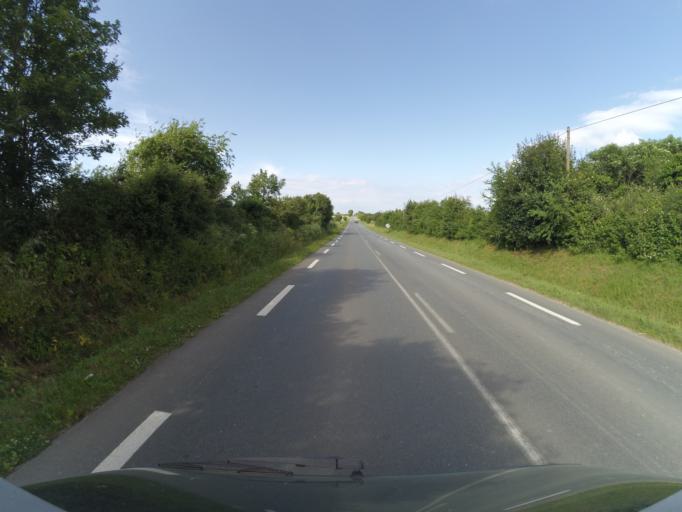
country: FR
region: Poitou-Charentes
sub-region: Departement de la Charente-Maritime
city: Saint-Xandre
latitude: 46.2277
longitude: -1.0808
